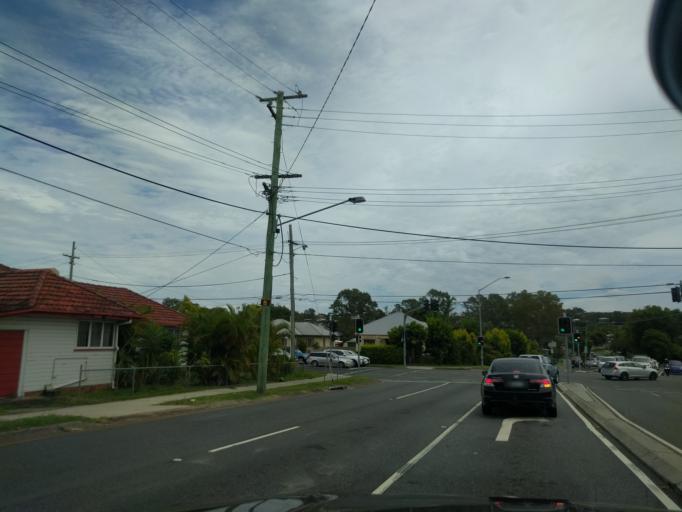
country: AU
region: Queensland
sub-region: Brisbane
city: Stafford
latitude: -27.4096
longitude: 153.0077
